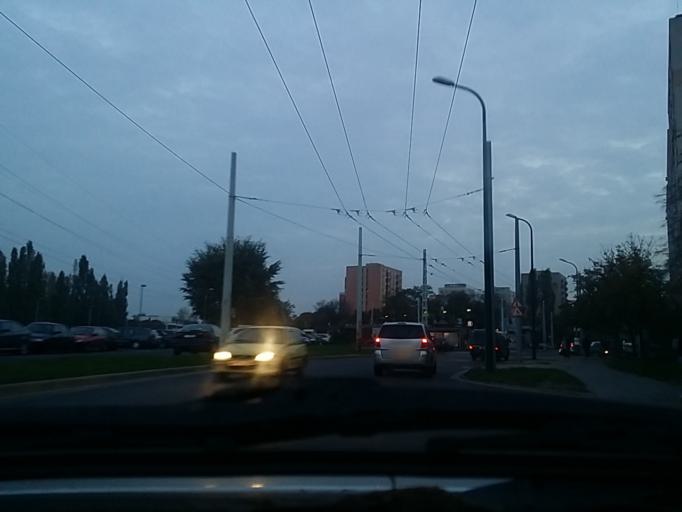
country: HU
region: Budapest
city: Budapest XVI. keruelet
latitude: 47.5139
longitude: 19.1459
